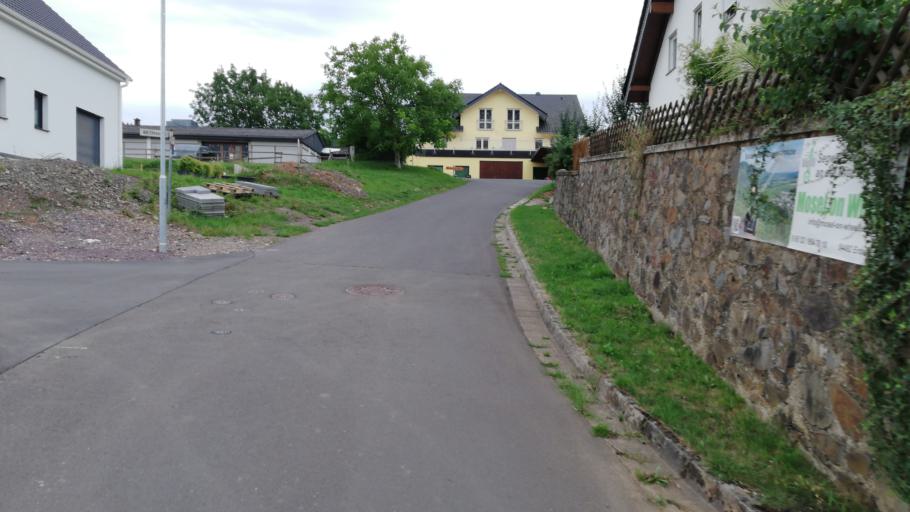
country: DE
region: Rheinland-Pfalz
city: Erden
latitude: 49.9780
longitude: 7.0255
